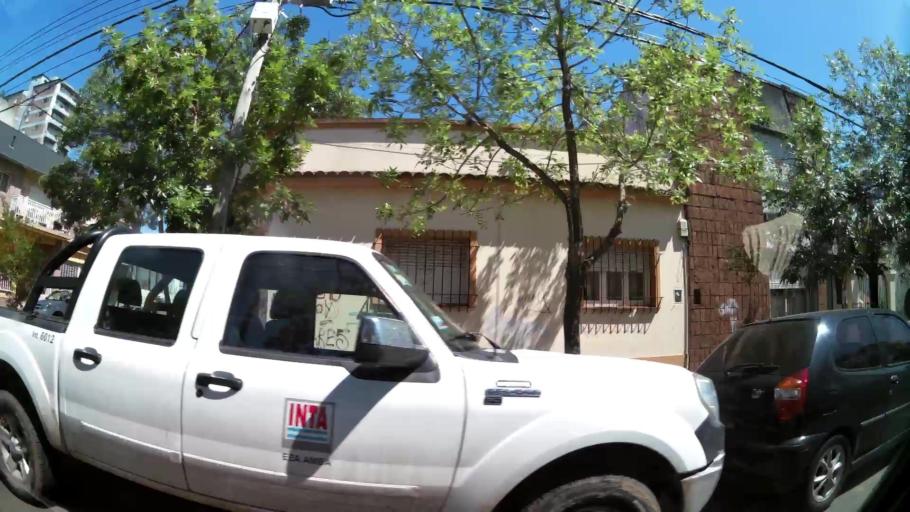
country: AR
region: Buenos Aires
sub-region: Partido de Tigre
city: Tigre
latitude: -34.4238
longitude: -58.5741
